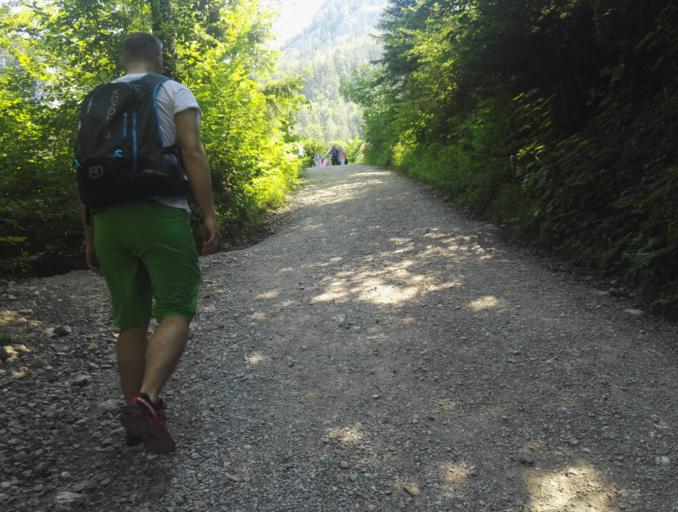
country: AT
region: Styria
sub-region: Politischer Bezirk Graz-Umgebung
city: Rothelstein
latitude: 47.3415
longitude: 15.3902
